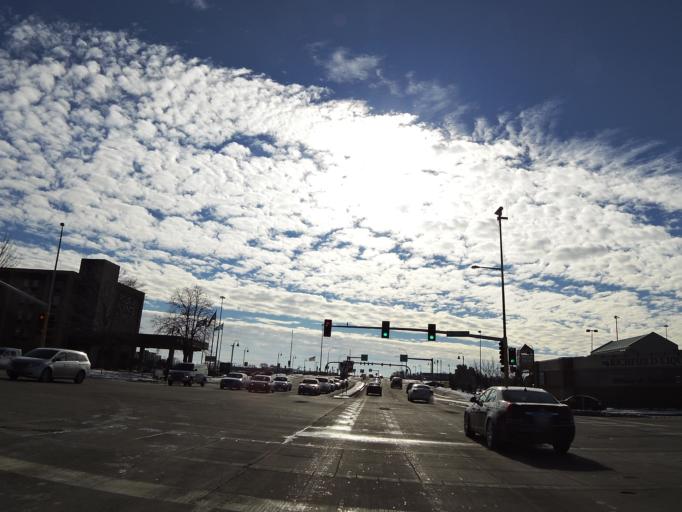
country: US
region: Minnesota
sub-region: Hennepin County
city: Richfield
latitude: 44.8641
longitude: -93.2885
